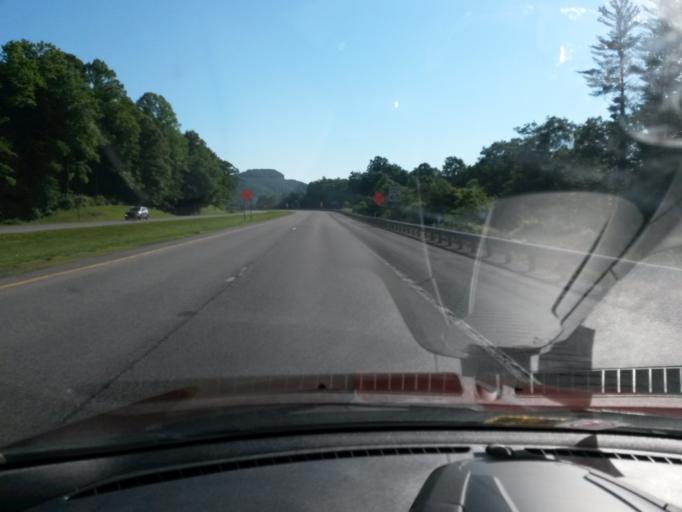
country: US
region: West Virginia
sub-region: Nicholas County
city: Summersville
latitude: 38.3762
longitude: -80.8172
